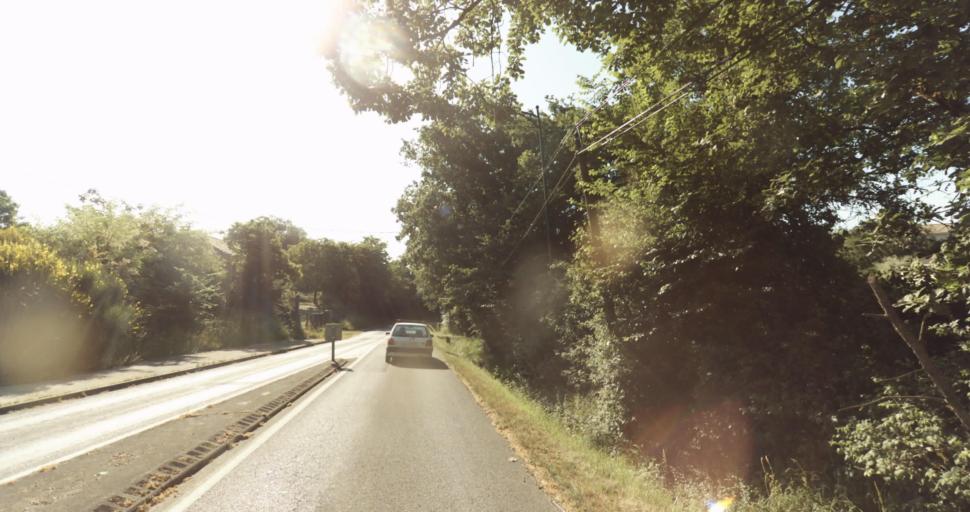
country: FR
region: Midi-Pyrenees
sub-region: Departement de la Haute-Garonne
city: La Salvetat-Saint-Gilles
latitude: 43.5675
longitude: 1.2810
